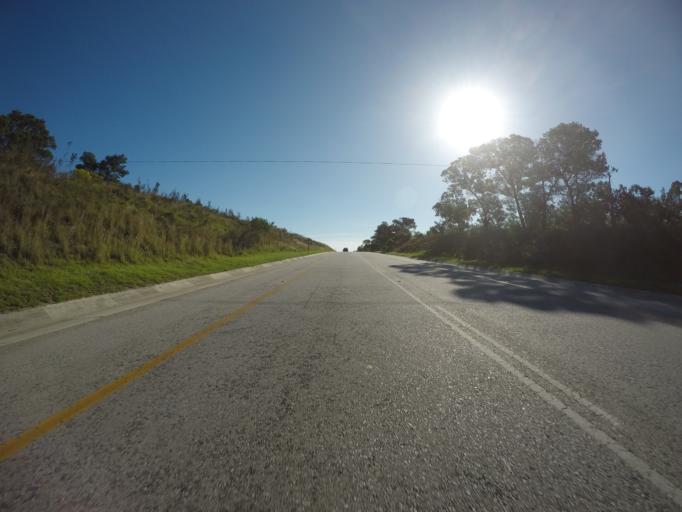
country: ZA
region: Eastern Cape
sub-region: Cacadu District Municipality
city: Jeffrey's Bay
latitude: -33.8931
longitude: 25.1447
